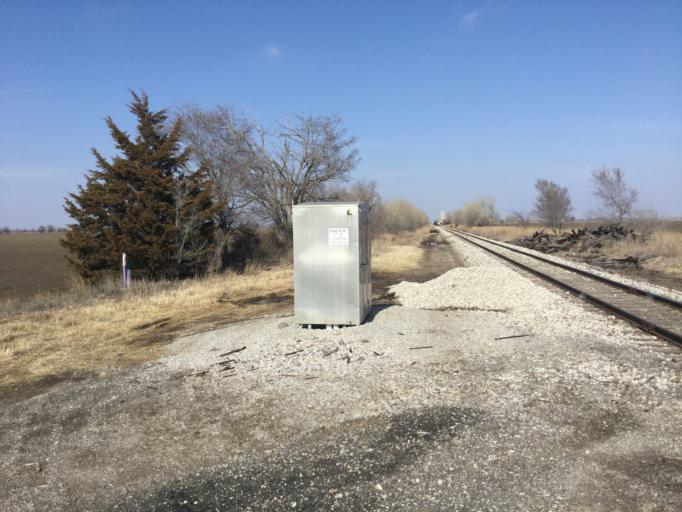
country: US
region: Kansas
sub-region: Sedgwick County
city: Haysville
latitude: 37.5637
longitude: -97.4363
